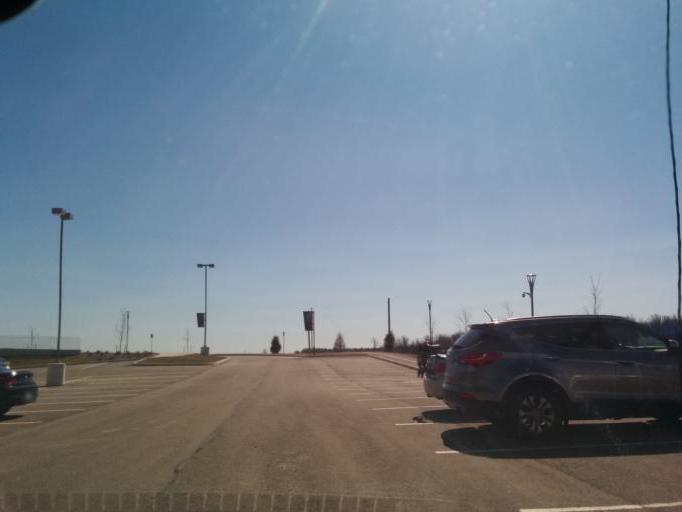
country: CA
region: Ontario
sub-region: Halton
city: Milton
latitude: 43.4738
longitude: -79.8772
